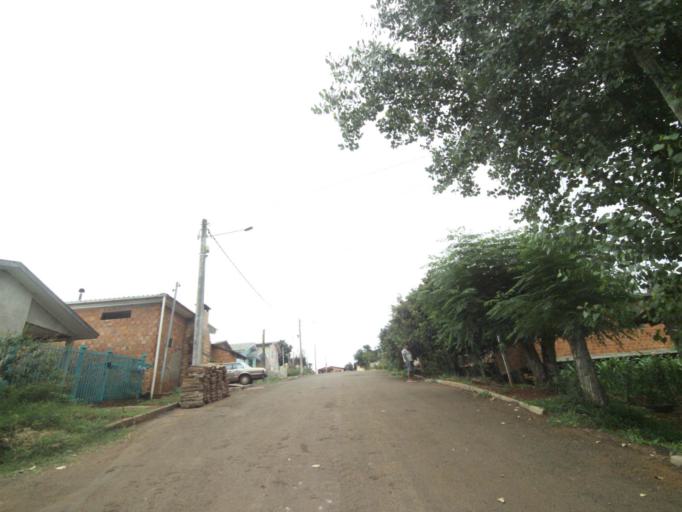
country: BR
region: Rio Grande do Sul
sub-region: Lagoa Vermelha
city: Lagoa Vermelha
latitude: -28.2149
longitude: -51.5074
